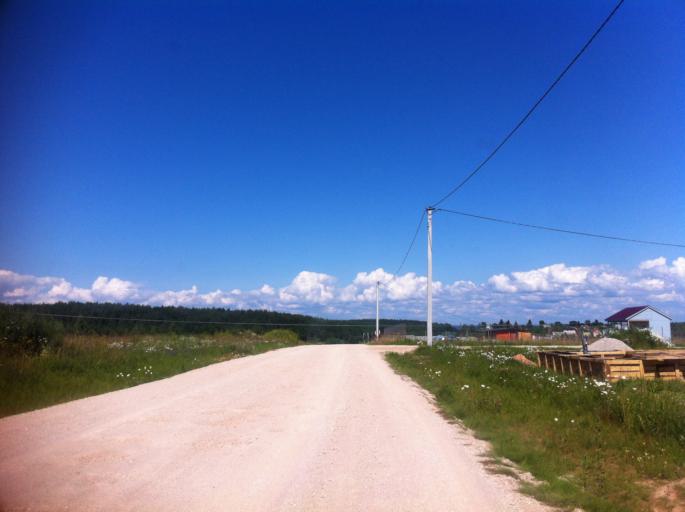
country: RU
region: Pskov
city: Izborsk
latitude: 57.8301
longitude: 27.9639
